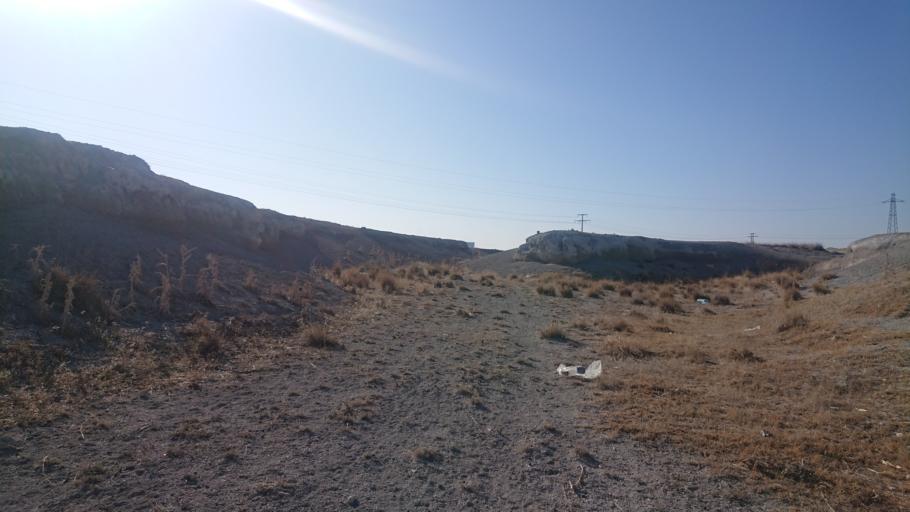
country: TR
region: Aksaray
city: Sultanhani
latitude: 38.2585
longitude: 33.5092
